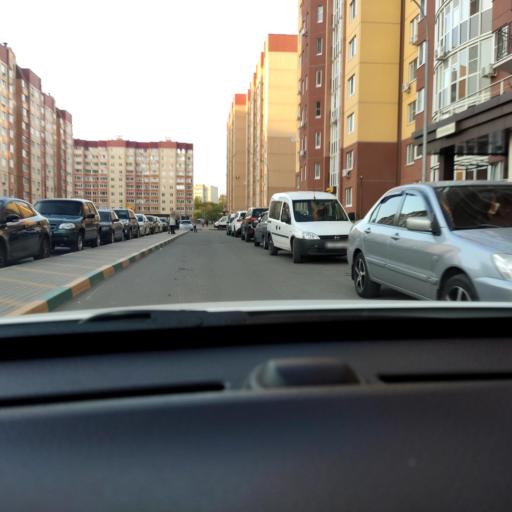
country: RU
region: Voronezj
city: Voronezh
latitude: 51.7163
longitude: 39.2658
